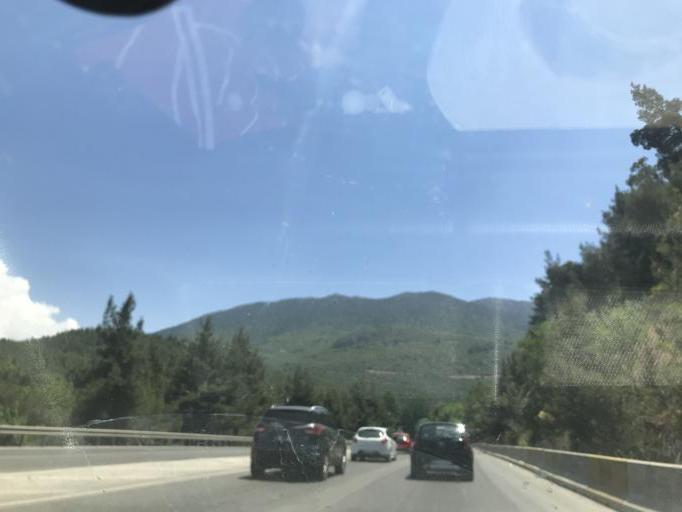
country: TR
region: Denizli
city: Denizli
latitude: 37.7301
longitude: 29.1651
